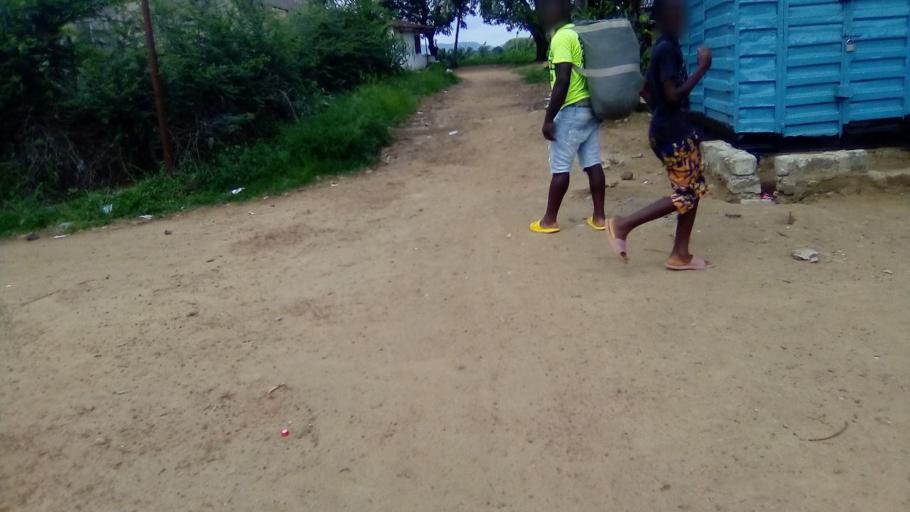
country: SL
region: Southern Province
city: Bo
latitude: 7.9587
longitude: -11.7195
